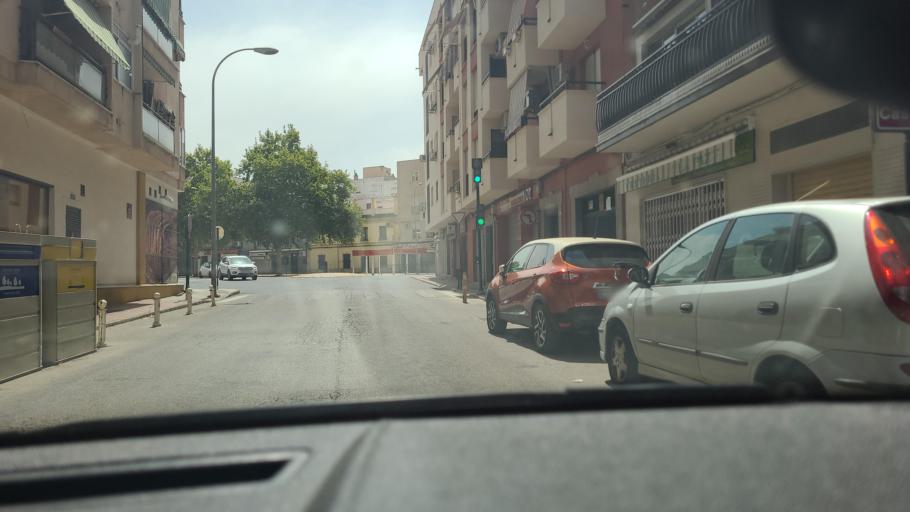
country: ES
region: Andalusia
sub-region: Provincia de Jaen
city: Linares
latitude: 38.0907
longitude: -3.6294
